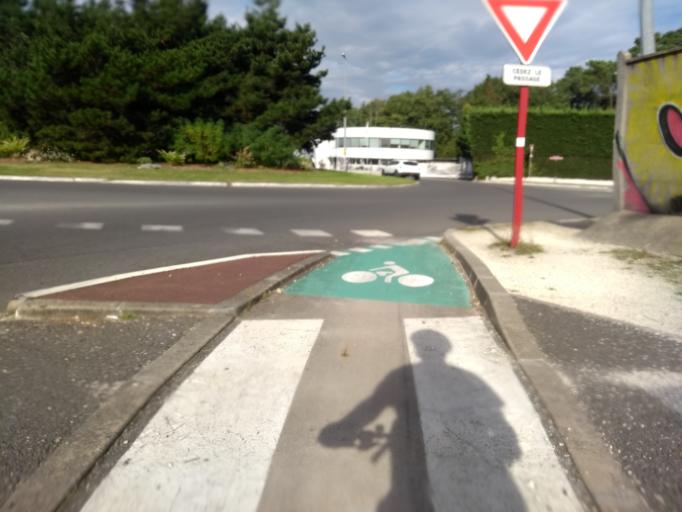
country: FR
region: Aquitaine
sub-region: Departement de la Gironde
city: Canejan
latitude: 44.7849
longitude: -0.6339
